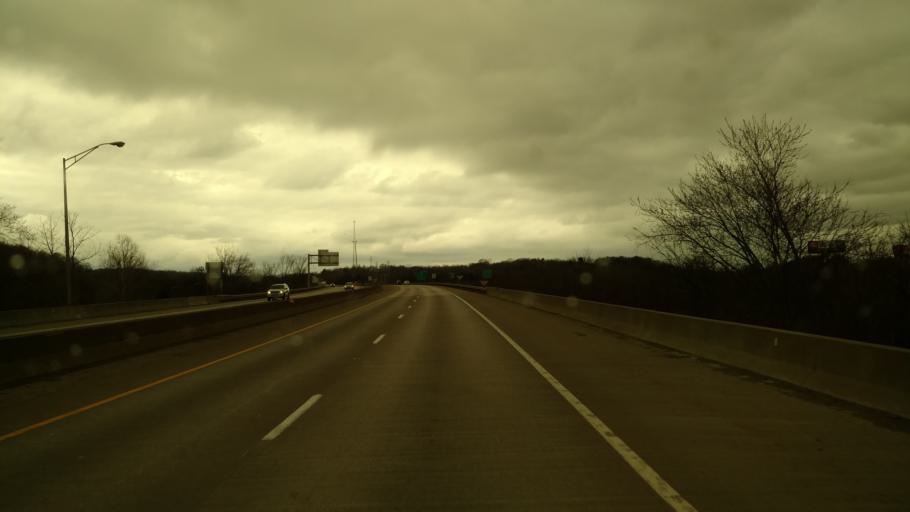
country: US
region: Ohio
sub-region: Muskingum County
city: Zanesville
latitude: 39.9490
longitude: -82.0228
